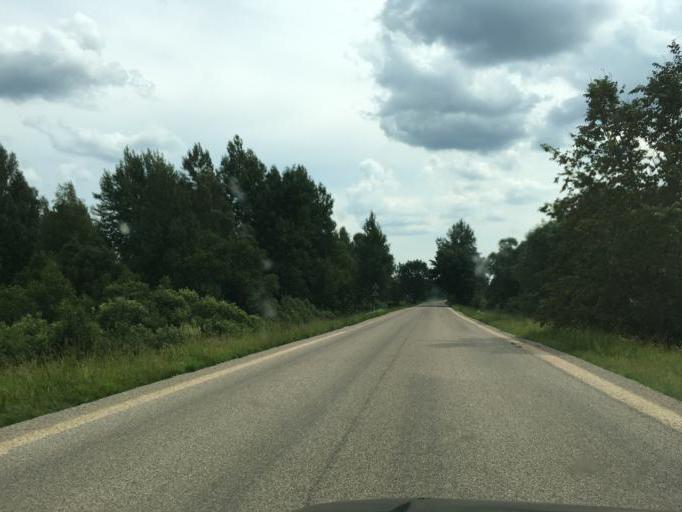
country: LV
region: Rugaju
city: Rugaji
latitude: 56.8456
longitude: 27.0918
